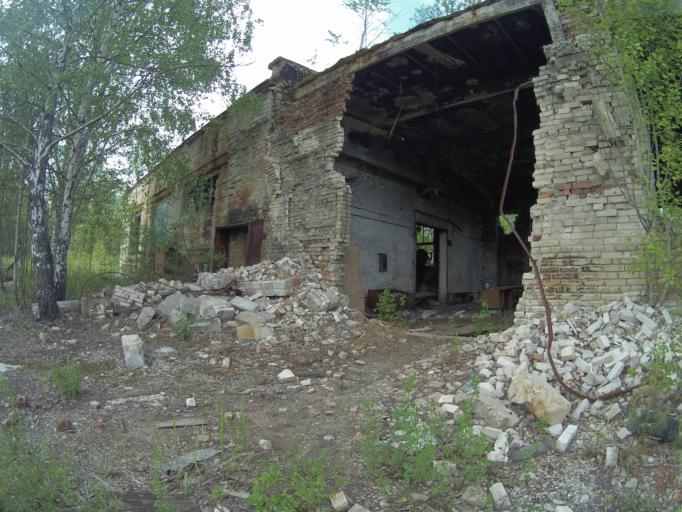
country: RU
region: Vladimir
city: Raduzhnyy
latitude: 55.9767
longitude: 40.2653
